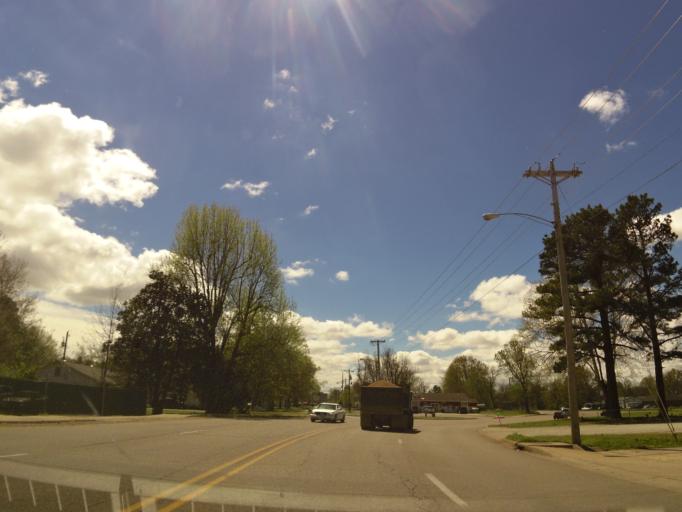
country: US
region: Arkansas
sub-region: Craighead County
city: Jonesboro
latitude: 35.8536
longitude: -90.7035
